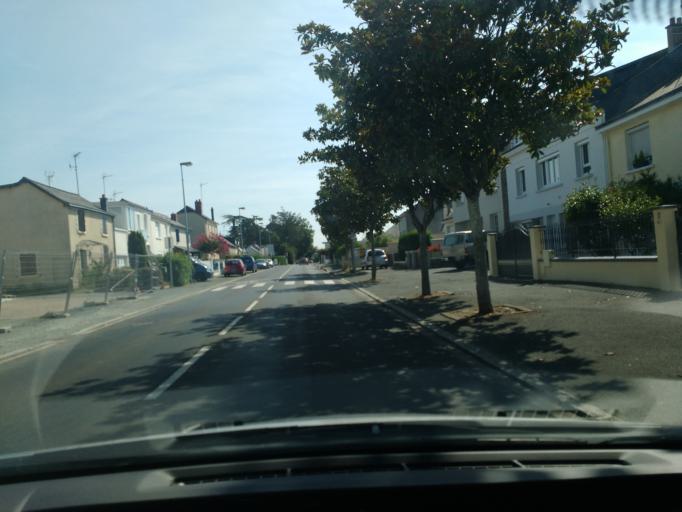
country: FR
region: Pays de la Loire
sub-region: Departement de Maine-et-Loire
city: Trelaze
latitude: 47.4668
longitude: -0.4924
